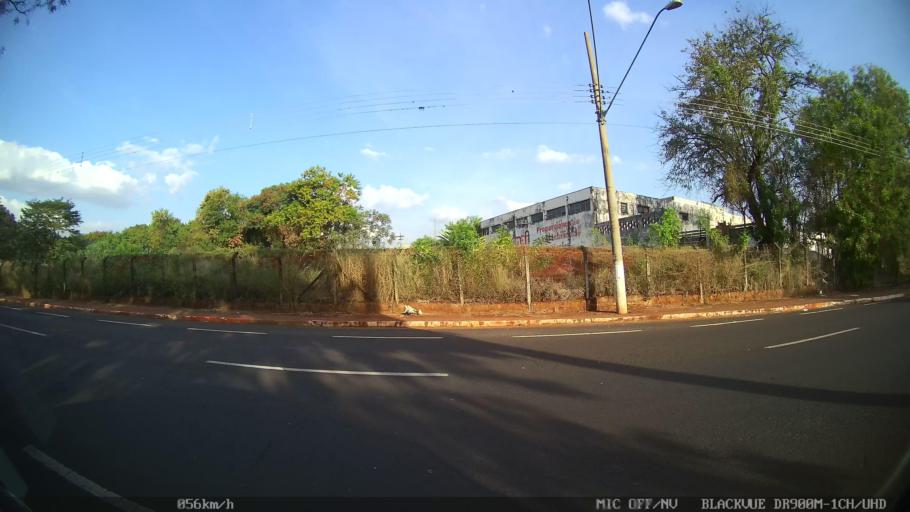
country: BR
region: Sao Paulo
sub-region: Ribeirao Preto
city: Ribeirao Preto
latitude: -21.1597
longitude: -47.8125
